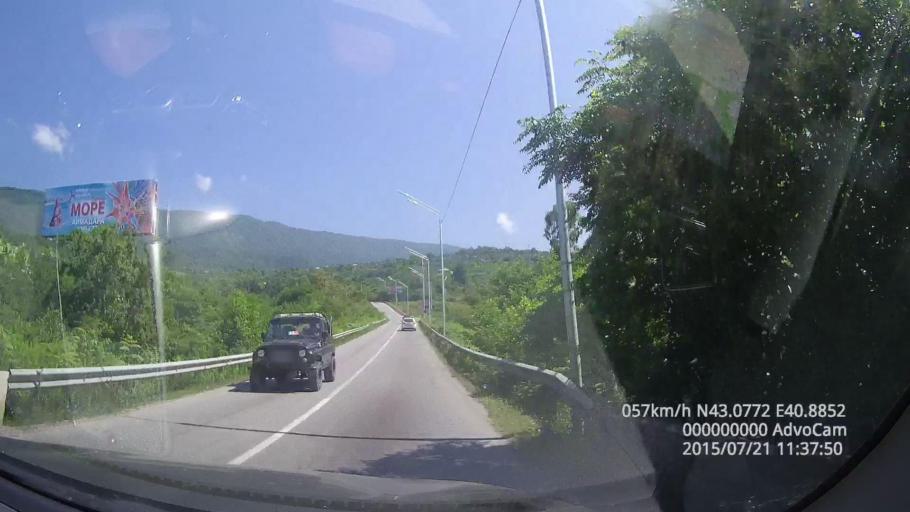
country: GE
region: Abkhazia
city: Stantsiya Novyy Afon
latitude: 43.0774
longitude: 40.8856
